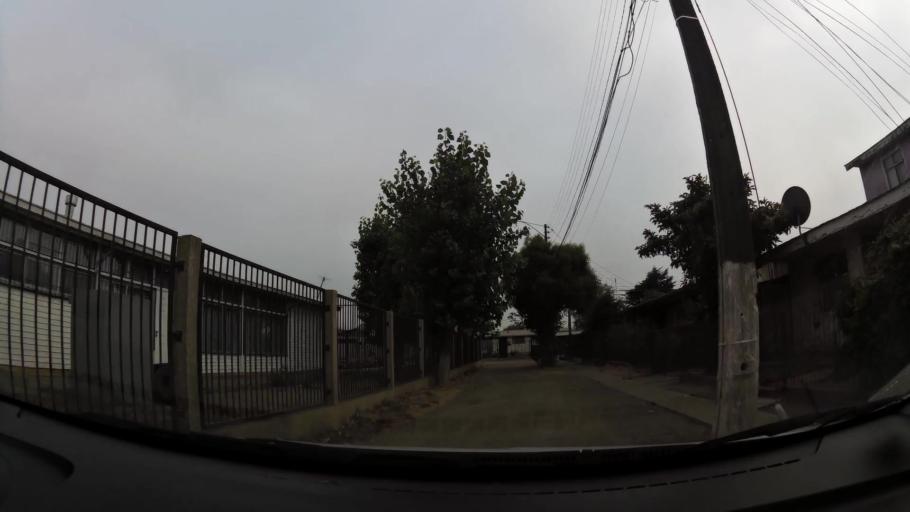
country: CL
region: Biobio
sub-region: Provincia de Concepcion
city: Concepcion
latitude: -36.7941
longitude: -73.0923
